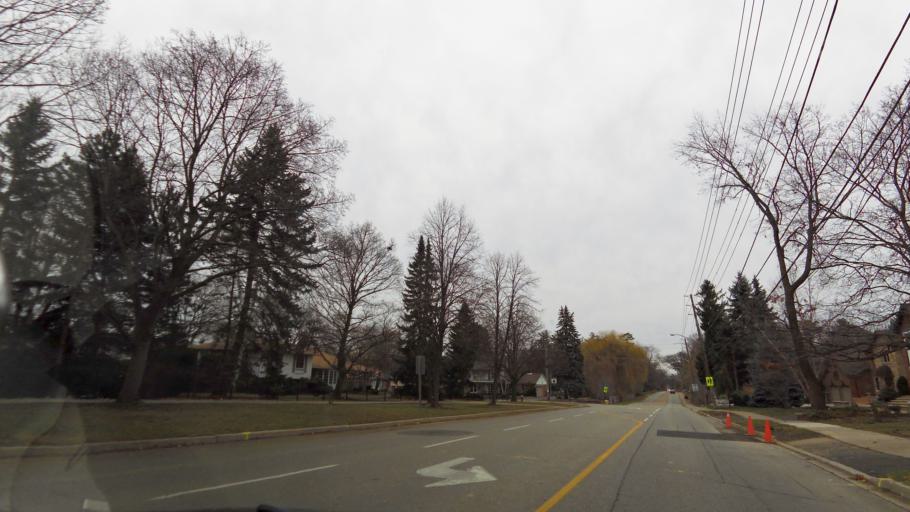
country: CA
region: Ontario
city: Mississauga
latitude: 43.5258
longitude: -79.6355
